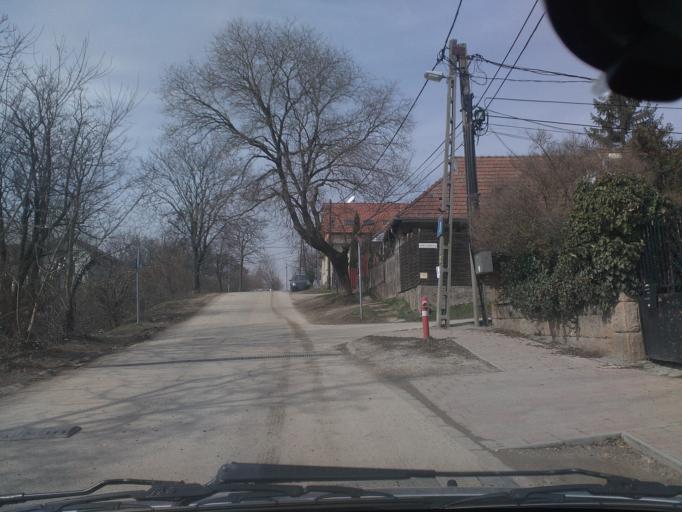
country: HU
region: Pest
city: Pilisborosjeno
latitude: 47.6100
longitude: 18.9894
